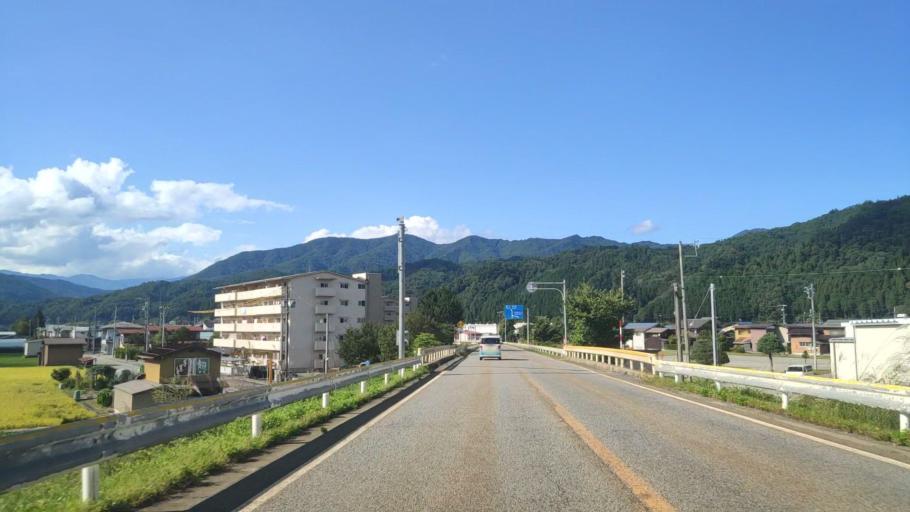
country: JP
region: Gifu
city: Takayama
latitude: 36.2504
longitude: 137.1629
